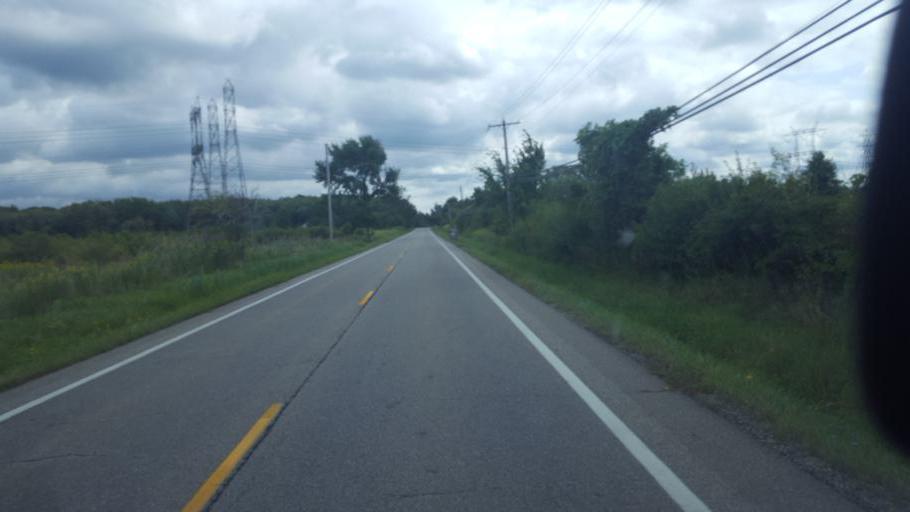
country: US
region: Ohio
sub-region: Geauga County
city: Chardon
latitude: 41.6636
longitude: -81.1448
